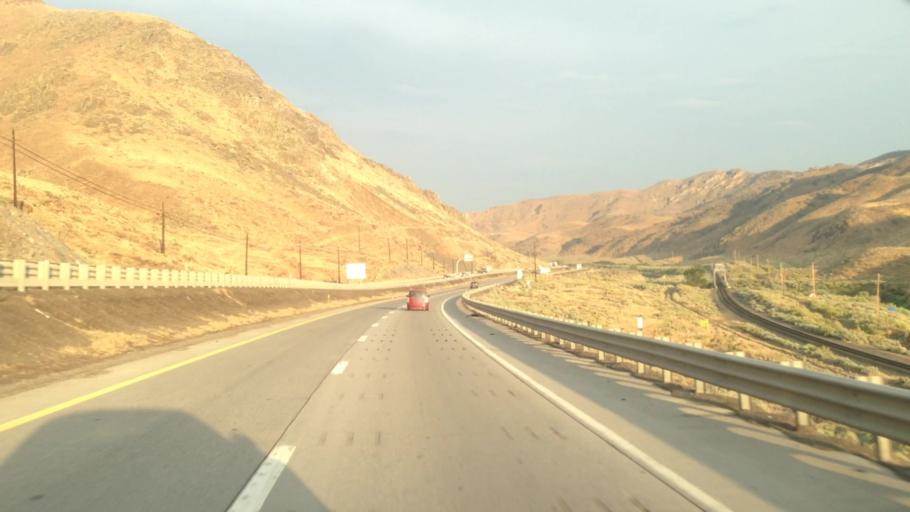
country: US
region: Nevada
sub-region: Washoe County
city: Sparks
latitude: 39.5224
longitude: -119.6894
